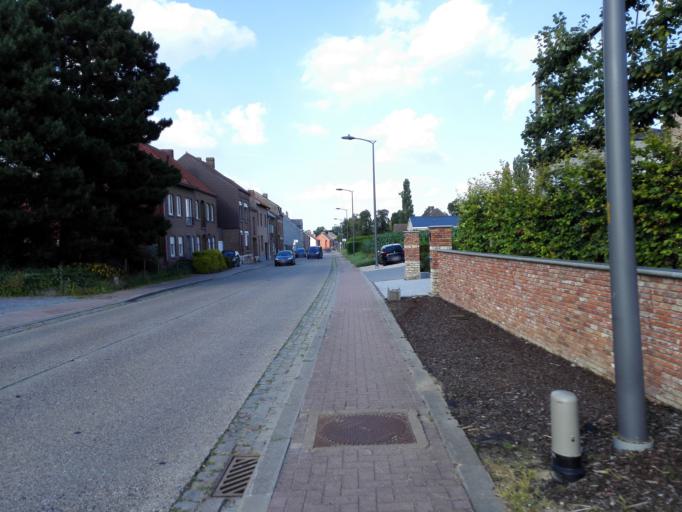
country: BE
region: Flanders
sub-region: Provincie Vlaams-Brabant
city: Tienen
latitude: 50.8272
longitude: 4.9814
